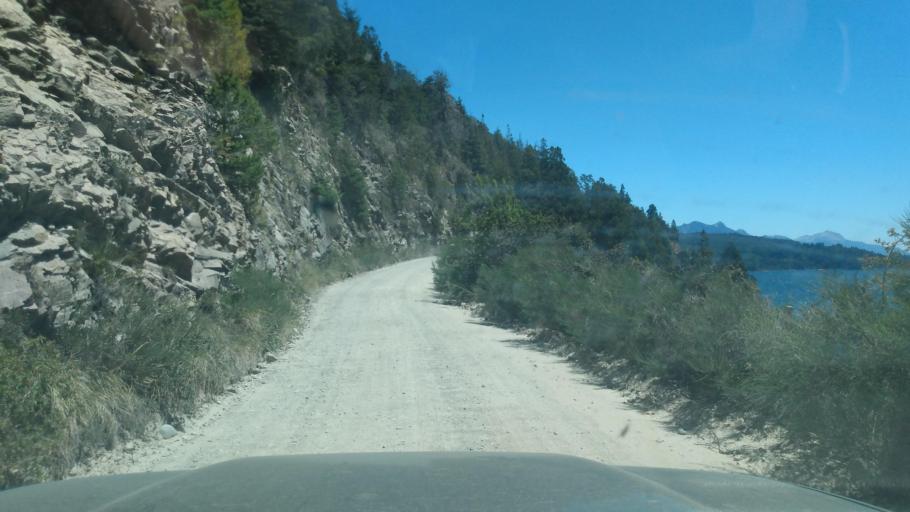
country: AR
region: Rio Negro
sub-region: Departamento de Bariloche
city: San Carlos de Bariloche
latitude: -41.1043
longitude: -71.4860
